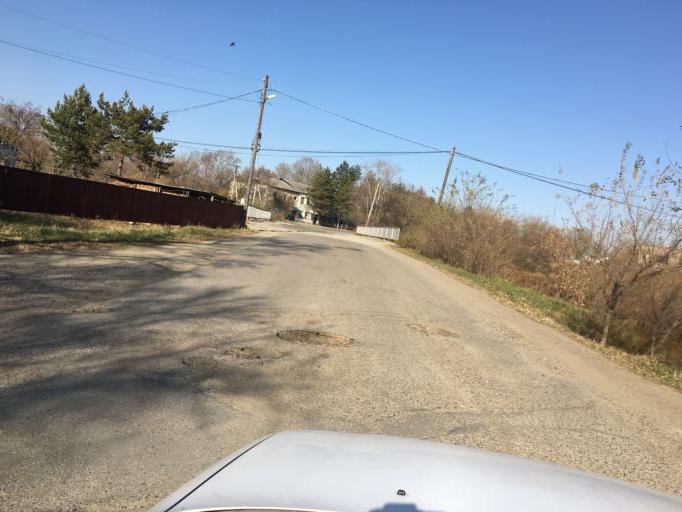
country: RU
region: Primorskiy
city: Dal'nerechensk
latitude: 45.9245
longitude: 133.7260
